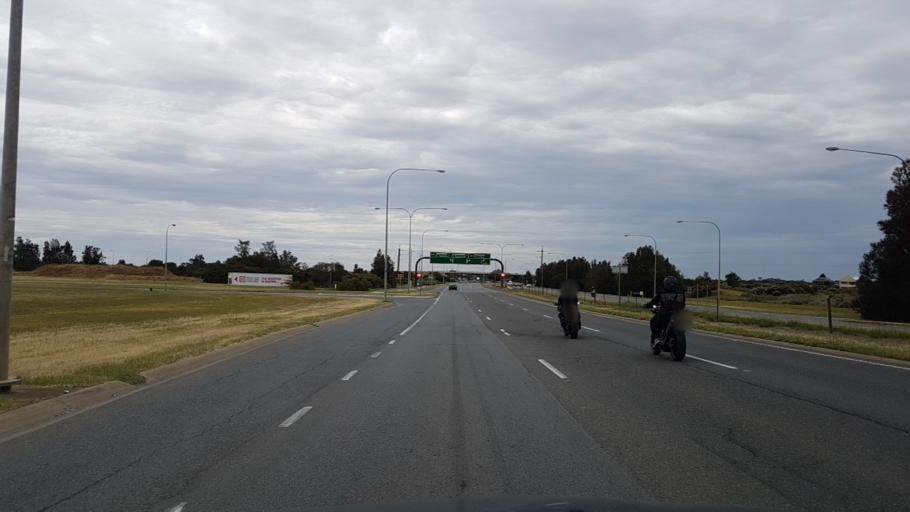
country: AU
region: South Australia
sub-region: Port Adelaide Enfield
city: Enfield
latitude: -34.8171
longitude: 138.5977
